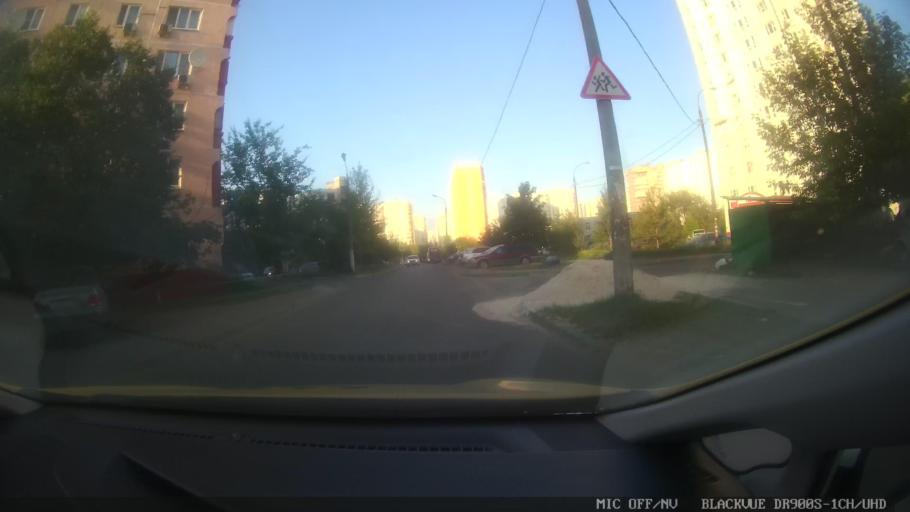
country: RU
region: Moscow
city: Nekrasovka
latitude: 55.6937
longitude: 37.9042
